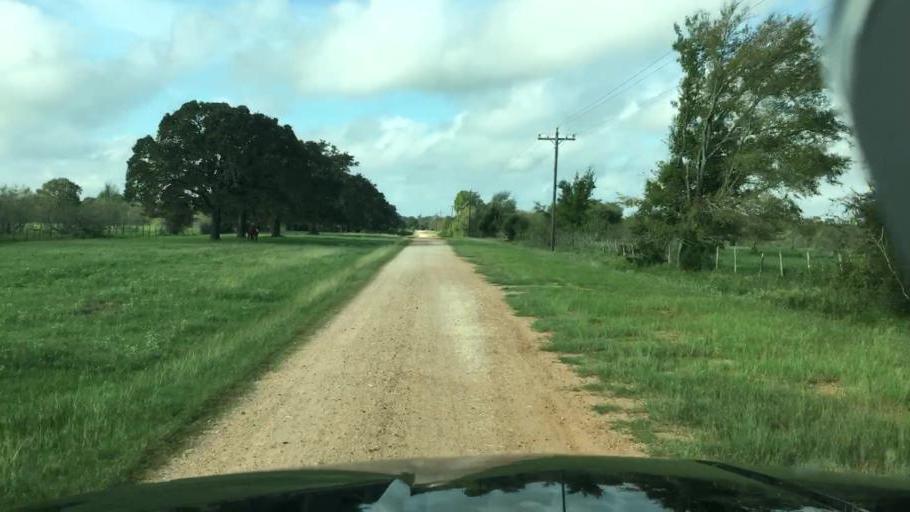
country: US
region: Texas
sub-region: Burleson County
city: Somerville
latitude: 30.3002
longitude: -96.7337
